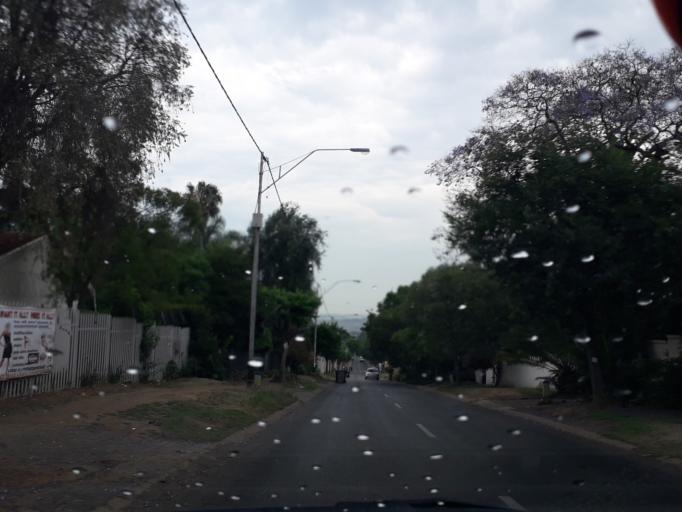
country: ZA
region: Gauteng
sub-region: City of Johannesburg Metropolitan Municipality
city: Modderfontein
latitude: -26.1297
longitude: 28.0898
